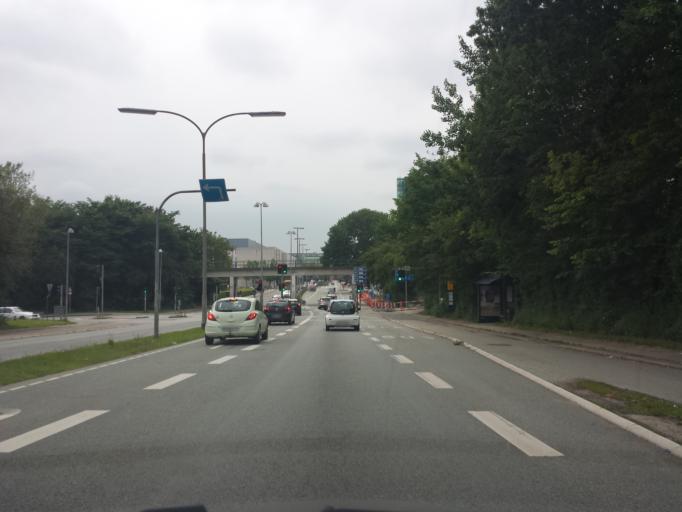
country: DK
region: Capital Region
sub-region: Lyngby-Tarbaek Kommune
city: Kongens Lyngby
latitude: 55.7733
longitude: 12.5113
